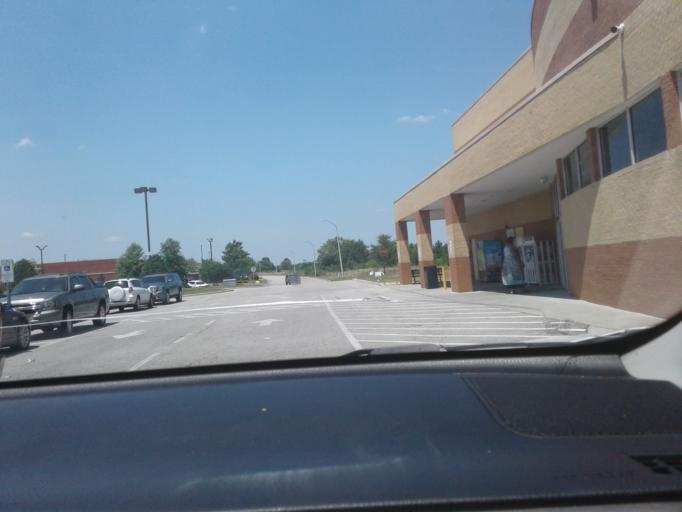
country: US
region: North Carolina
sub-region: Harnett County
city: Dunn
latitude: 35.2919
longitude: -78.5951
